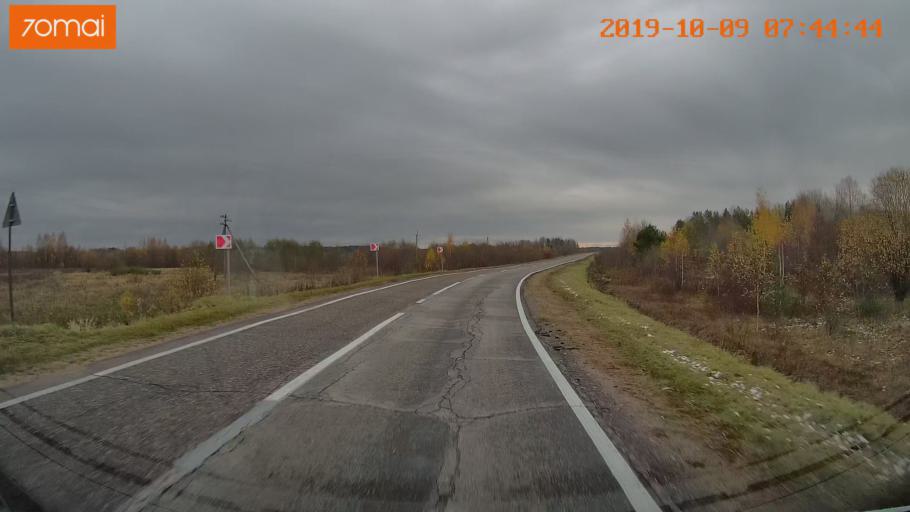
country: RU
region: Jaroslavl
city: Kukoboy
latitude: 58.6506
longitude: 39.7529
